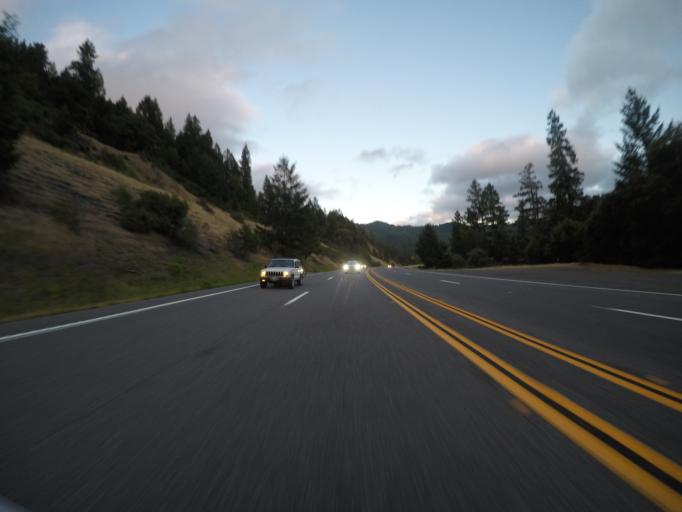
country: US
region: California
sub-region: Humboldt County
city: Redway
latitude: 40.0464
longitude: -123.7839
